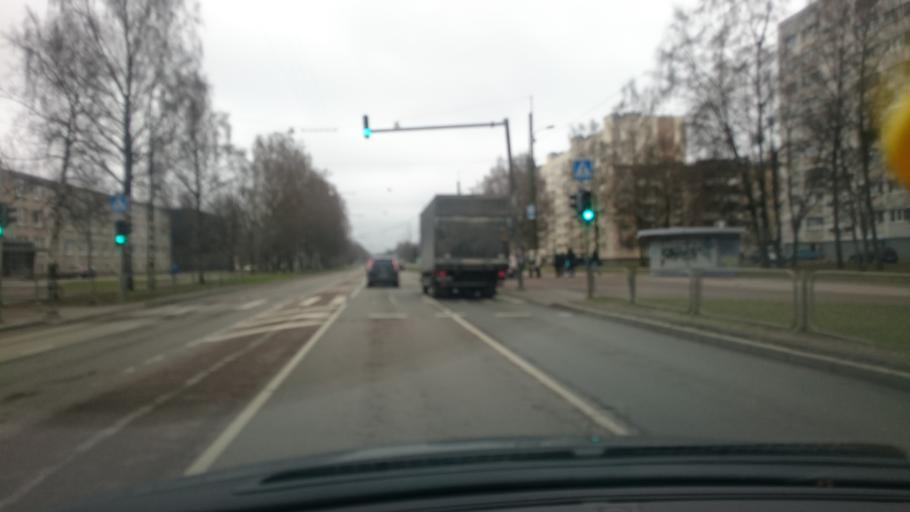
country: EE
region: Harju
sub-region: Tallinna linn
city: Tallinn
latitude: 59.4431
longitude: 24.7042
